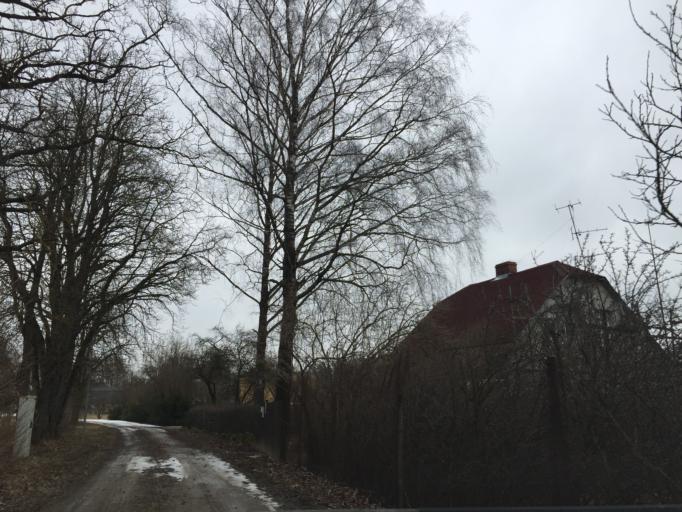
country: LV
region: Lielvarde
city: Lielvarde
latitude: 56.7527
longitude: 24.7811
